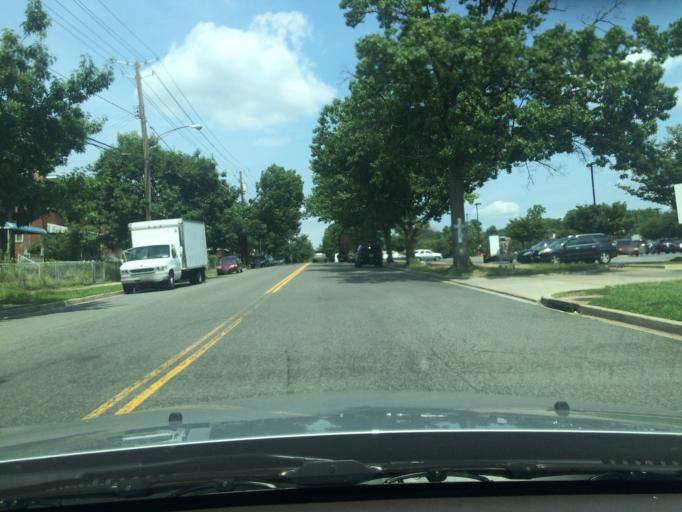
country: US
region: Maryland
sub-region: Prince George's County
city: Chillum
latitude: 38.9597
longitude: -76.9948
